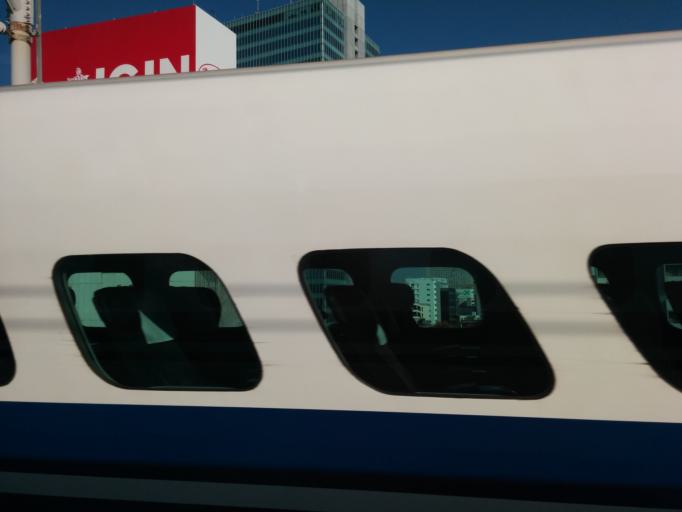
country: JP
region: Aichi
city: Nagoya-shi
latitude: 35.1644
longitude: 136.8849
